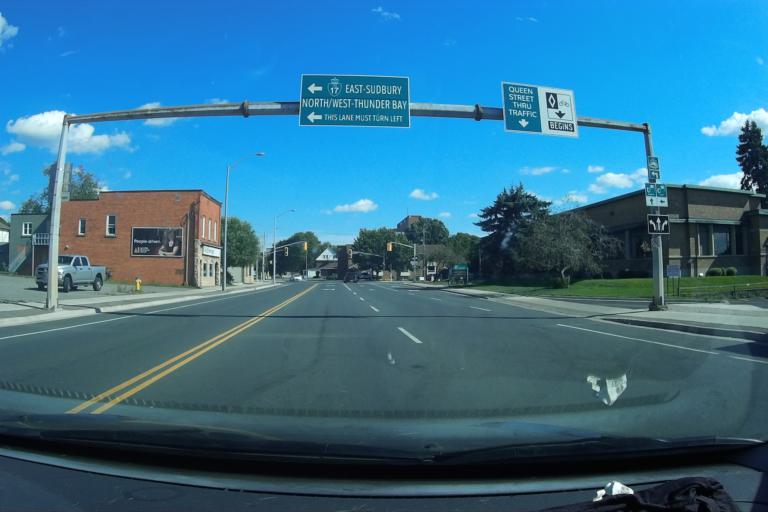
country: CA
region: Ontario
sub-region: Algoma
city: Sault Ste. Marie
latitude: 46.5061
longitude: -84.3231
